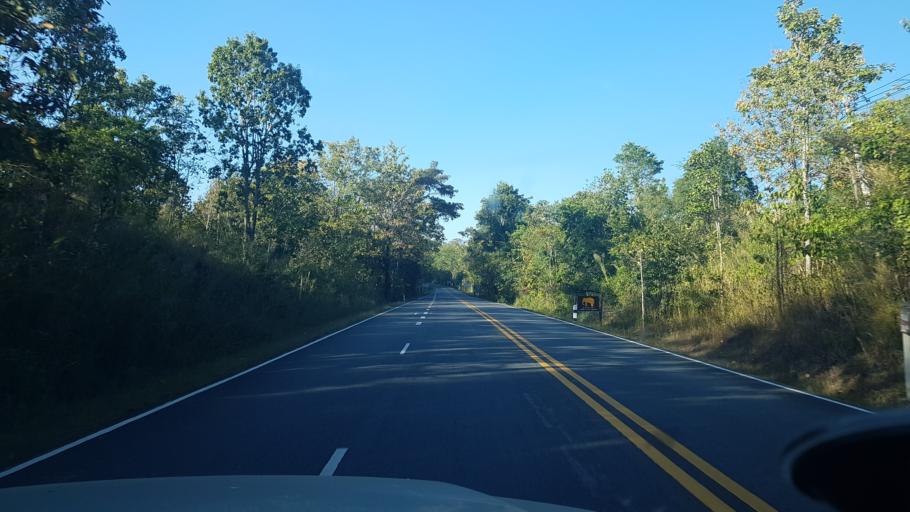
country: TH
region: Phetchabun
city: Nam Nao
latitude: 16.7015
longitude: 101.6444
